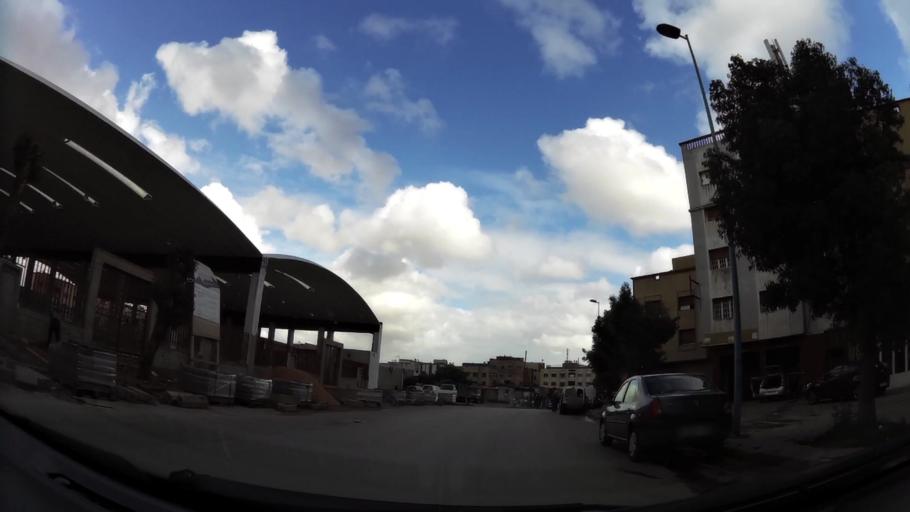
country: MA
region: Grand Casablanca
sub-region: Casablanca
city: Casablanca
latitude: 33.5465
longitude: -7.5875
